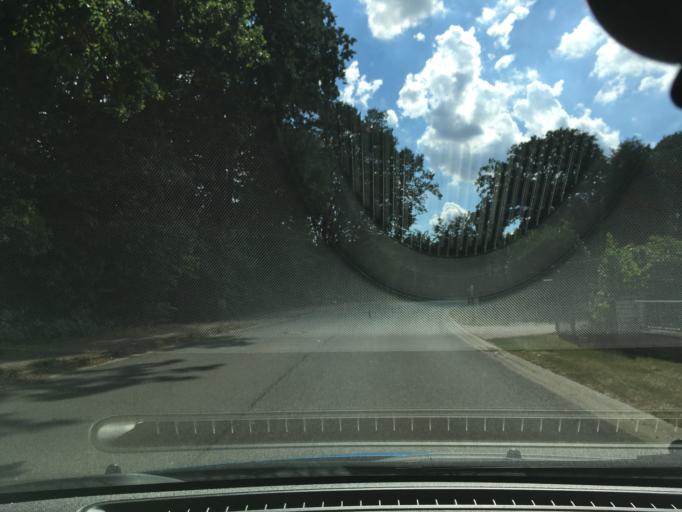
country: DE
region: Lower Saxony
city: Rehlingen
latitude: 53.1054
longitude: 10.2193
